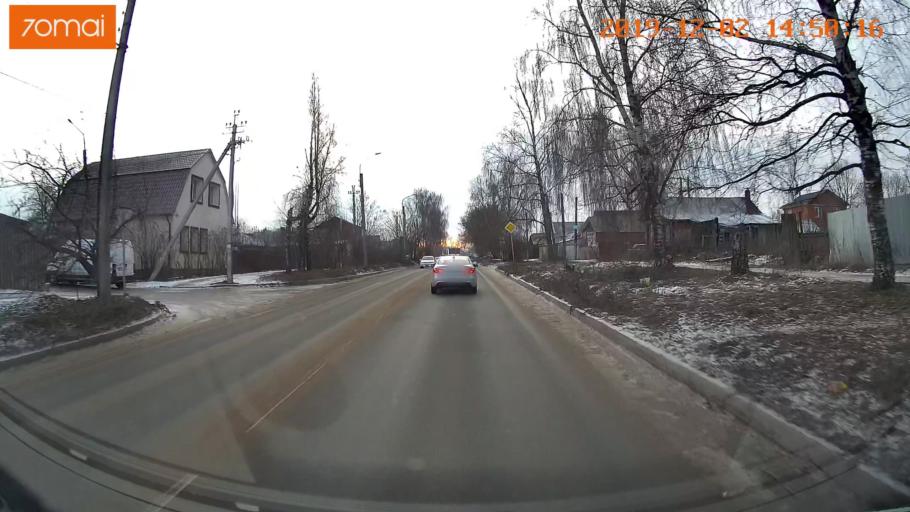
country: RU
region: Ivanovo
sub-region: Gorod Ivanovo
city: Ivanovo
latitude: 56.9811
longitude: 41.0068
